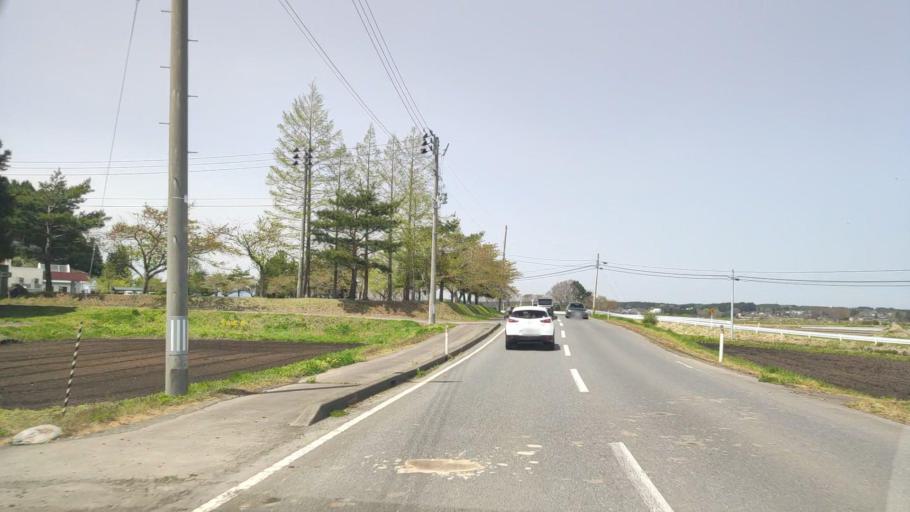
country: JP
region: Aomori
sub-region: Misawa Shi
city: Inuotose
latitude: 40.5930
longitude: 141.3425
